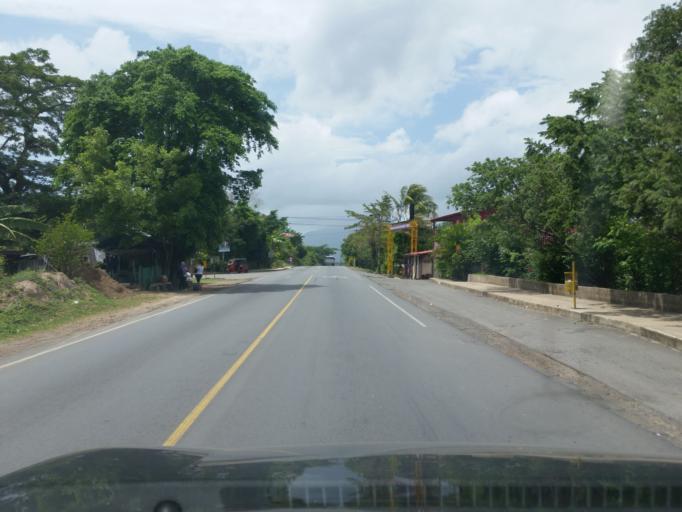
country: NI
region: Masaya
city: San Juan de Oriente
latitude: 11.9078
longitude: -86.0742
